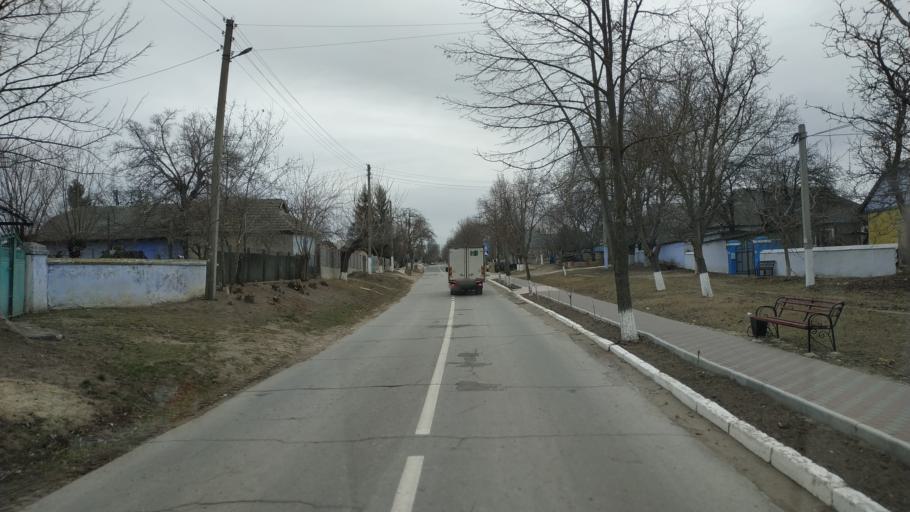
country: MD
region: Telenesti
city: Cocieri
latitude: 47.3447
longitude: 29.0922
